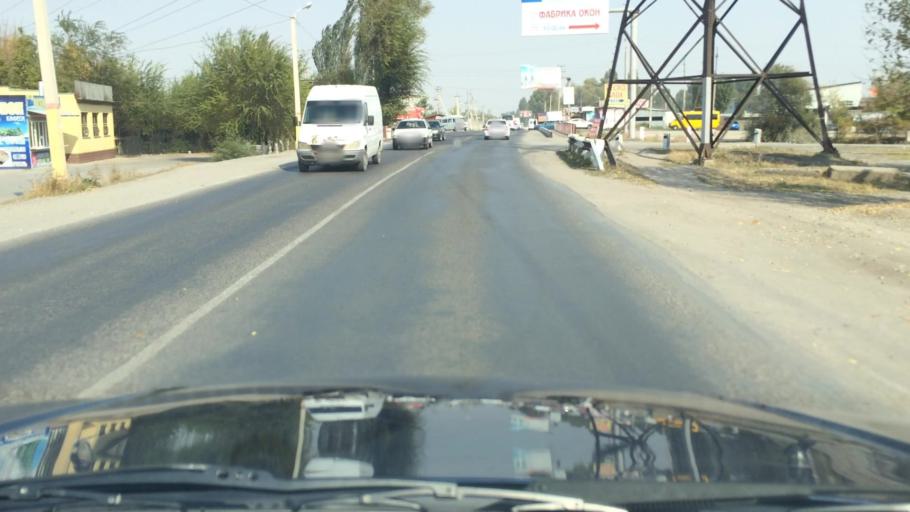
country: KG
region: Chuy
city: Lebedinovka
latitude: 42.8882
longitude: 74.6791
